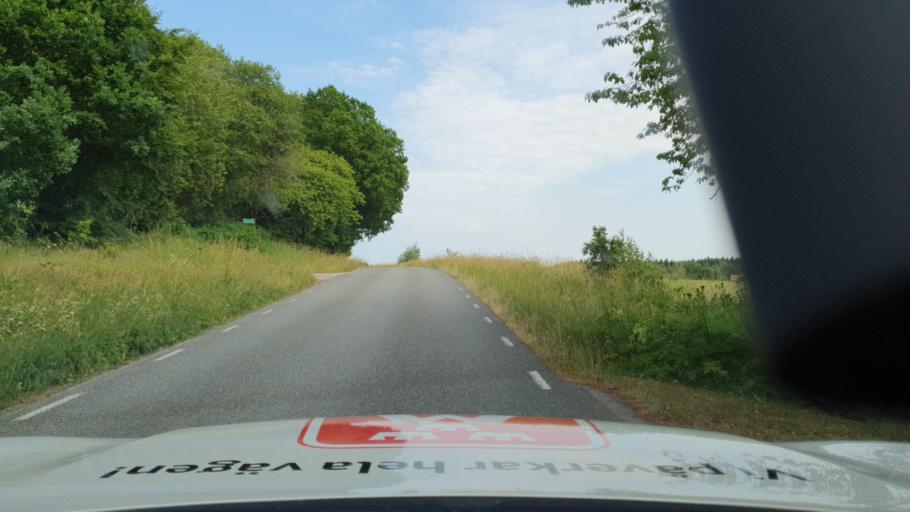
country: SE
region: Skane
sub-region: Kristianstads Kommun
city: Degeberga
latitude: 55.6979
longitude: 14.0586
